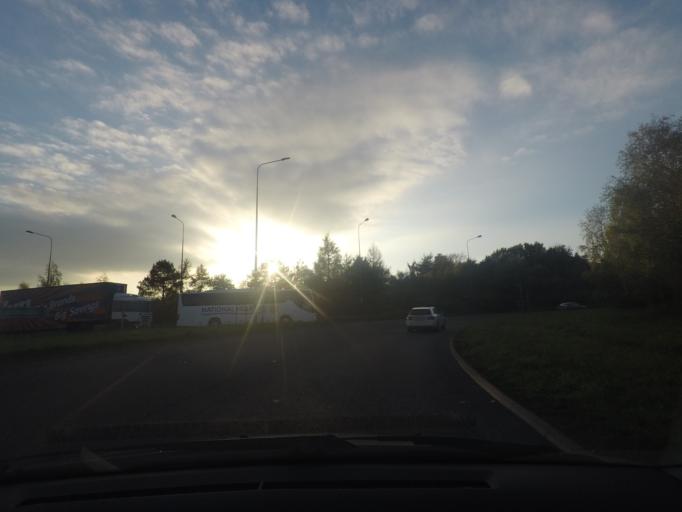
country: GB
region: England
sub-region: North Lincolnshire
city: Scawby
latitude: 53.5436
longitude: -0.5576
